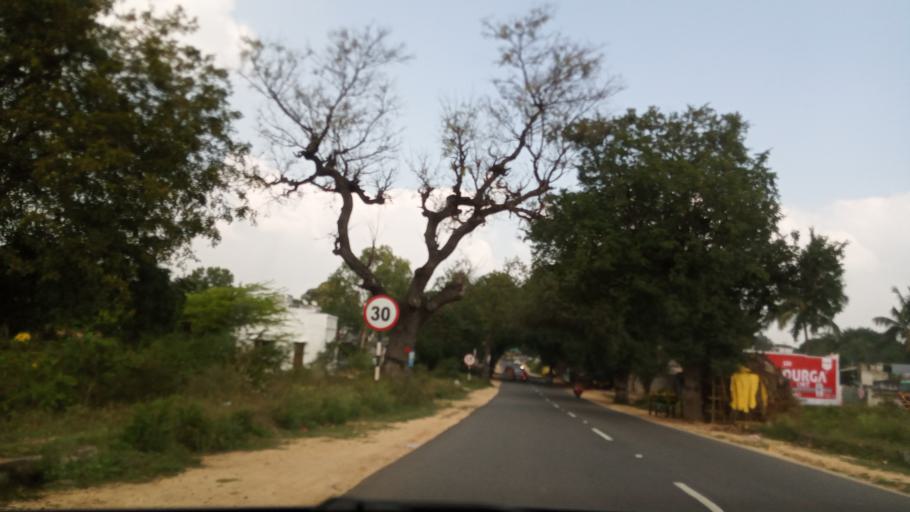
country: IN
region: Andhra Pradesh
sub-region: Chittoor
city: Madanapalle
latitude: 13.5915
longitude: 78.5260
